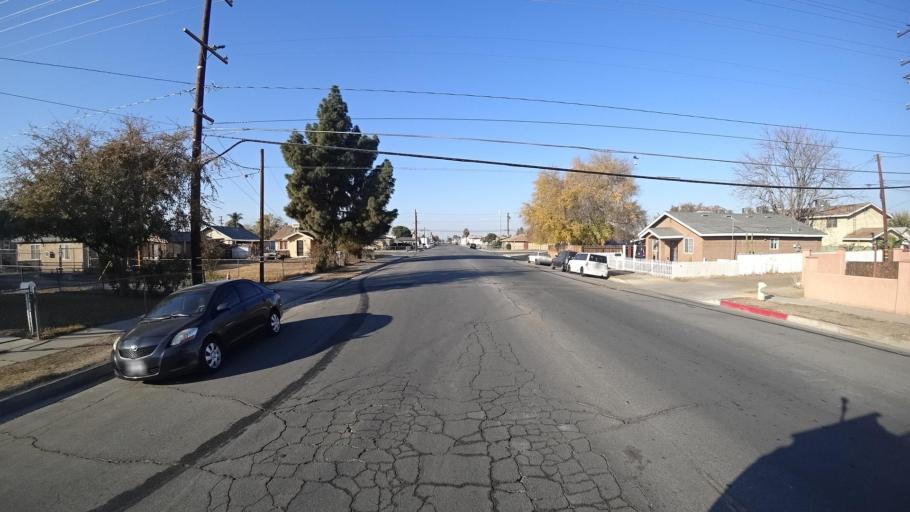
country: US
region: California
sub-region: Kern County
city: Delano
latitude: 35.7683
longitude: -119.2419
